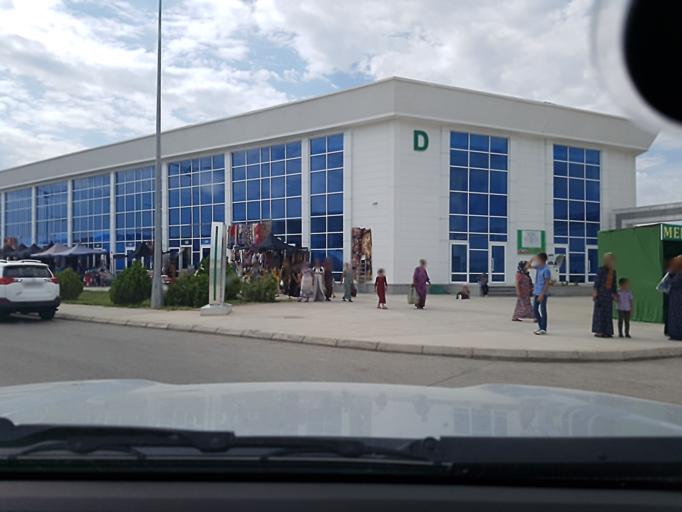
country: TM
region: Dasoguz
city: Dasoguz
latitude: 41.8771
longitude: 59.9496
